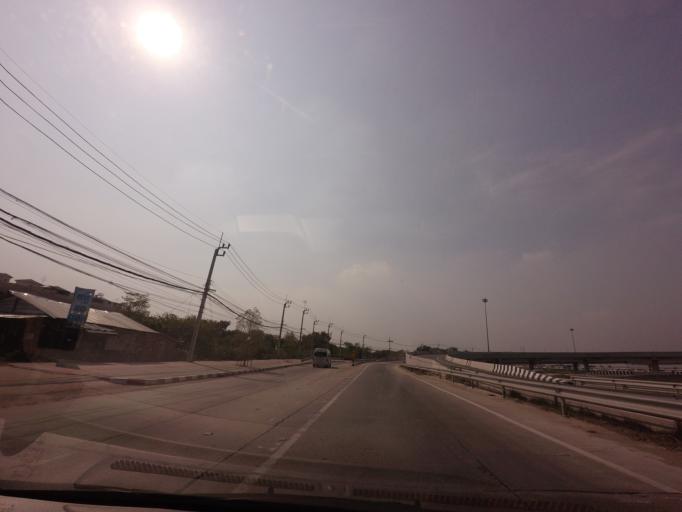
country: TH
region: Bangkok
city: Lat Krabang
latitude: 13.7546
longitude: 100.7455
